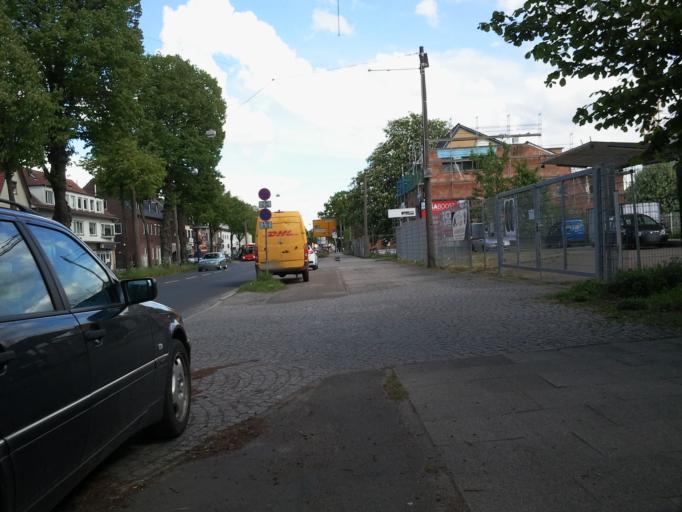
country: DE
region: Lower Saxony
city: Ritterhude
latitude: 53.1345
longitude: 8.7335
